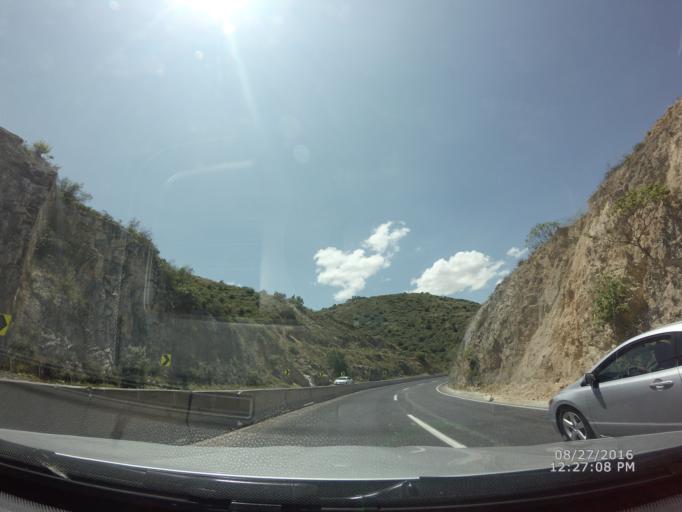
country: MX
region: Hidalgo
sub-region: Mineral de la Reforma
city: Colonia Militar
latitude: 20.1268
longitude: -98.6932
